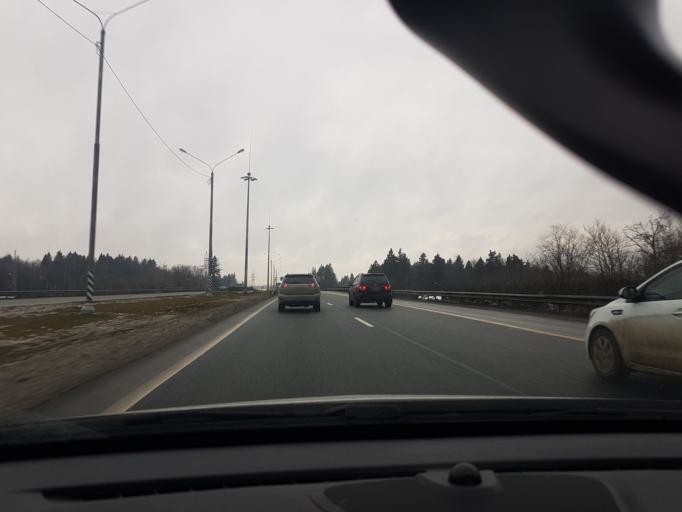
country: RU
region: Moskovskaya
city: Novopetrovskoye
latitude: 55.9802
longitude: 36.4532
